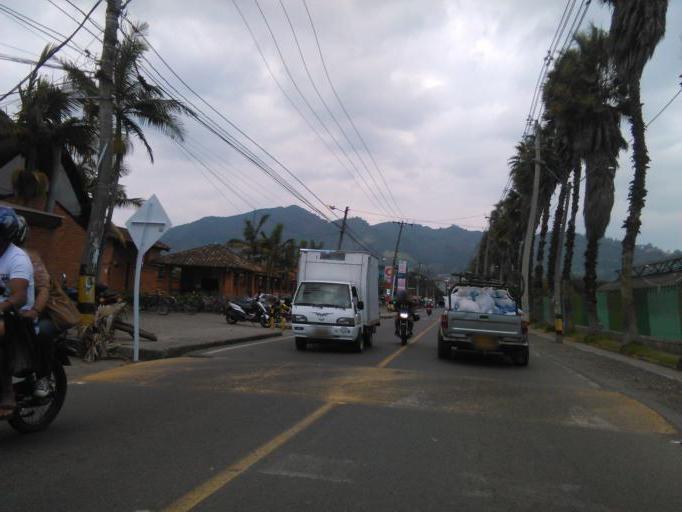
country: CO
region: Antioquia
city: La Ceja
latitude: 6.0286
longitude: -75.4261
